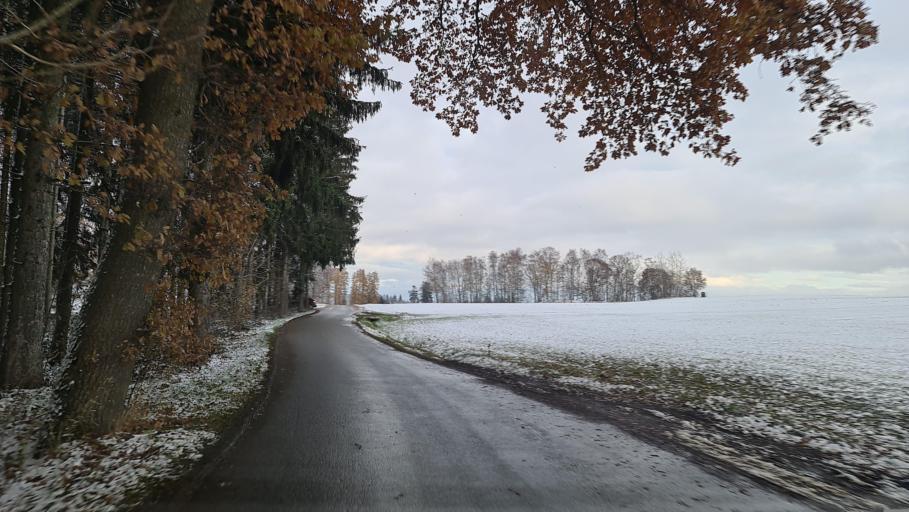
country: DE
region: Saxony
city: Zwonitz
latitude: 50.6443
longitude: 12.7877
